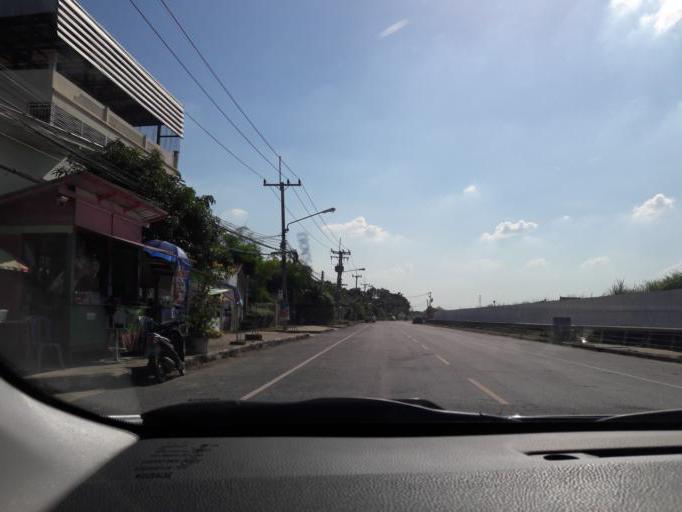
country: TH
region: Ang Thong
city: Ang Thong
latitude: 14.5876
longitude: 100.4511
